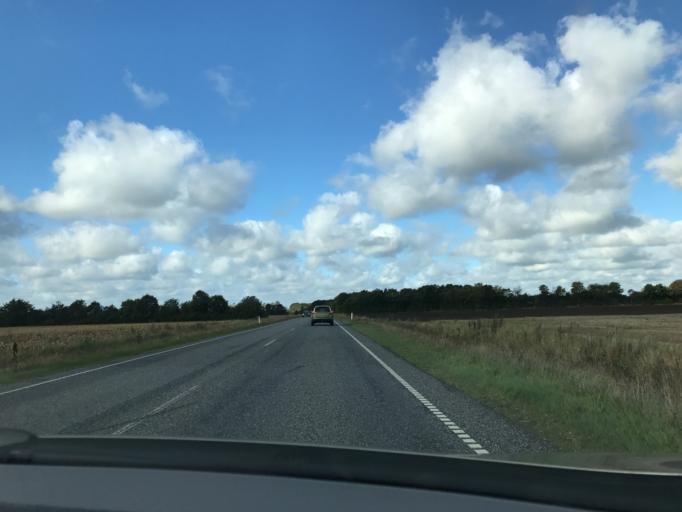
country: DK
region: South Denmark
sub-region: Billund Kommune
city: Billund
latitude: 55.7163
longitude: 9.1872
